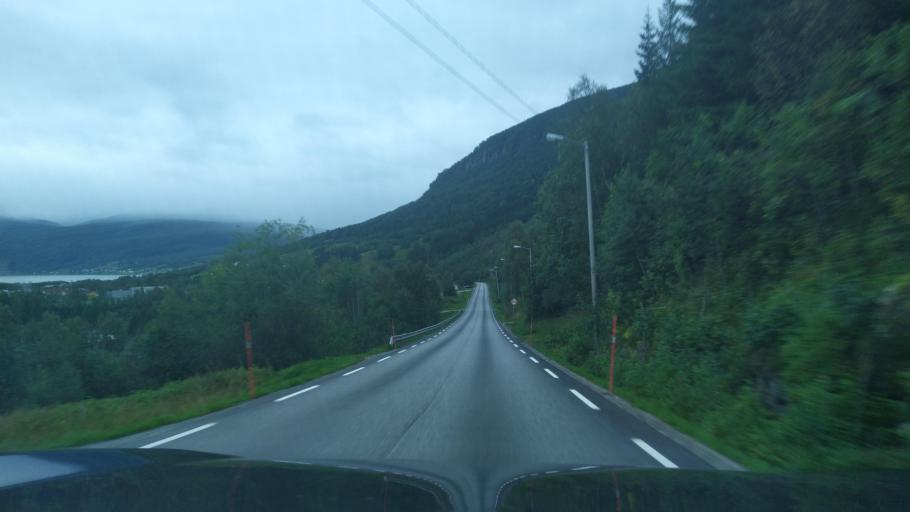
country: NO
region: Troms
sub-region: Lavangen
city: Tennevoll
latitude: 68.7411
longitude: 17.8157
